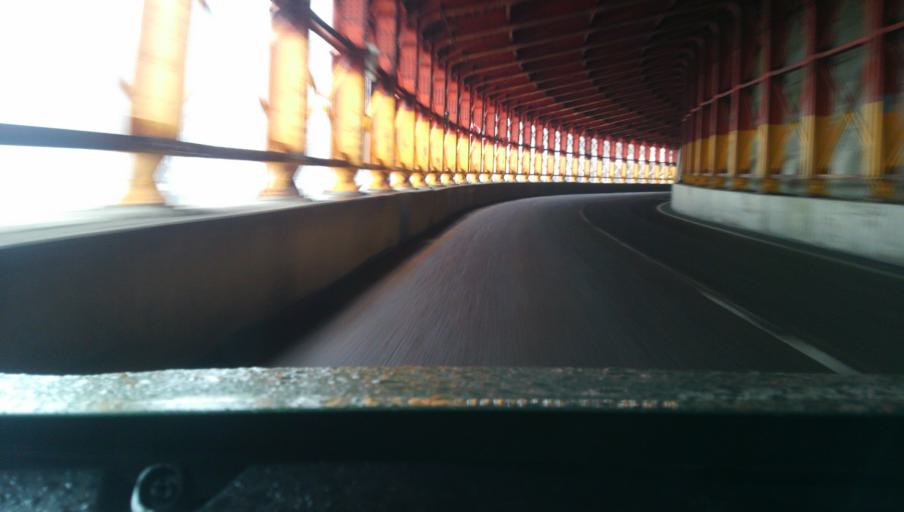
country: JP
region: Iwate
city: Kitakami
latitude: 39.3093
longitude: 140.8431
